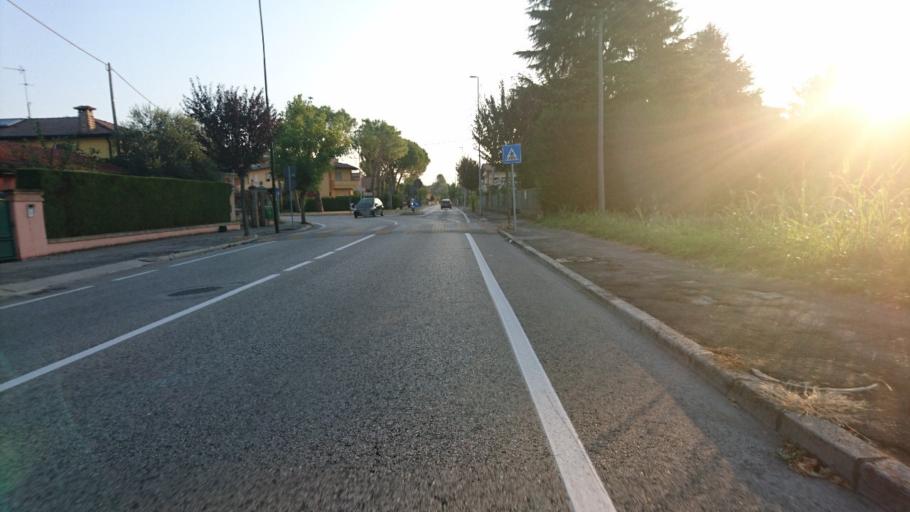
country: IT
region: Veneto
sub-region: Provincia di Padova
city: Ponte San Nicolo
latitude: 45.3689
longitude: 11.9396
